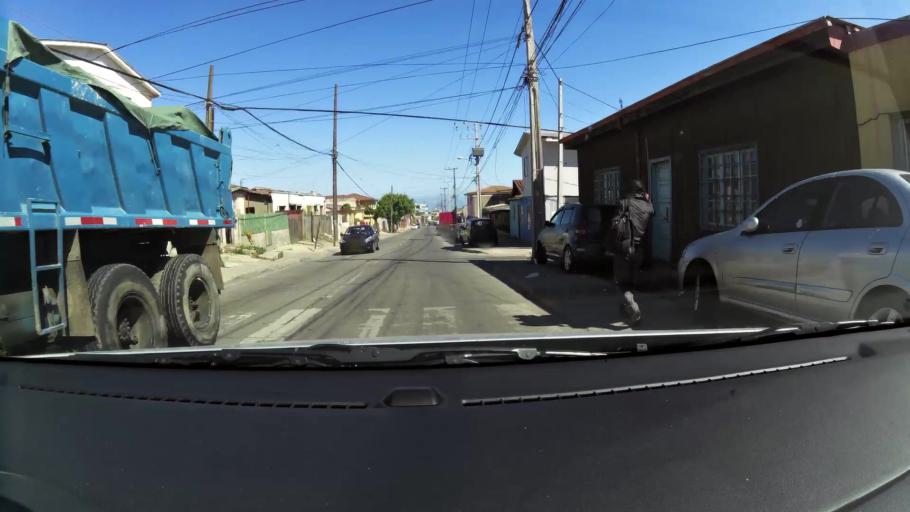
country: CL
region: Valparaiso
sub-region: Provincia de Valparaiso
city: Valparaiso
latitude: -33.0671
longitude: -71.5832
